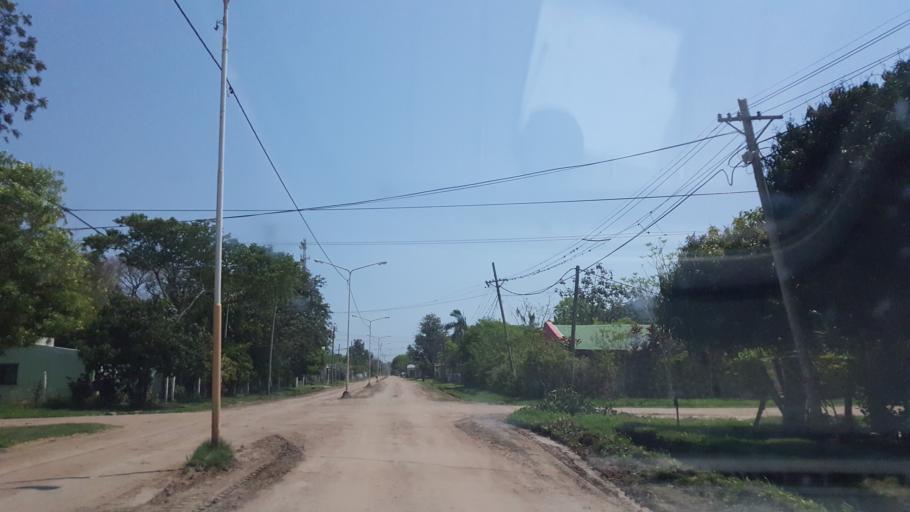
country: AR
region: Corrientes
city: Ita Ibate
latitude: -27.4261
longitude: -57.3331
